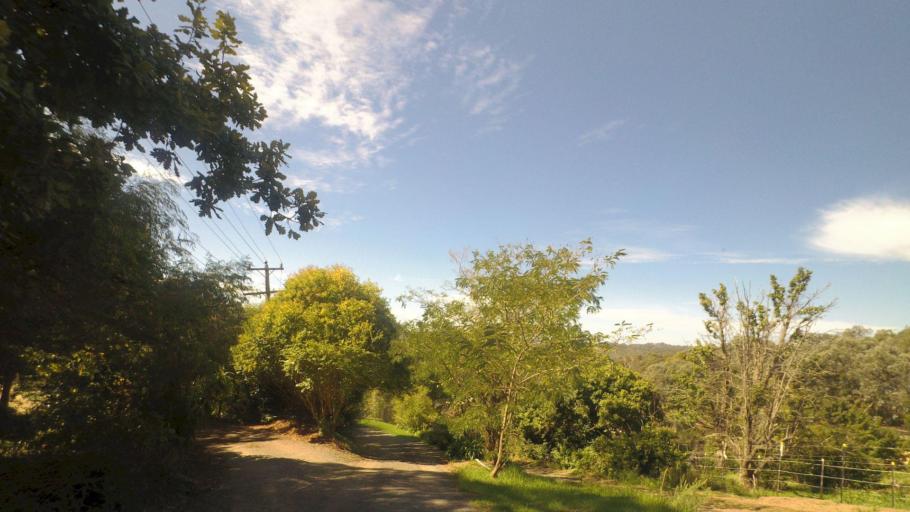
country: AU
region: Victoria
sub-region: Manningham
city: Warrandyte
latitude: -37.7413
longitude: 145.2254
